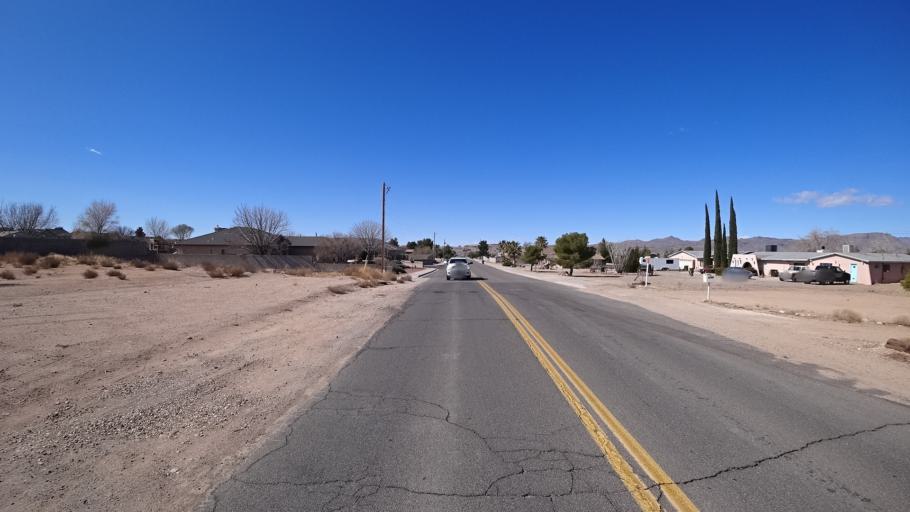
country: US
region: Arizona
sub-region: Mohave County
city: Kingman
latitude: 35.1958
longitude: -114.0067
